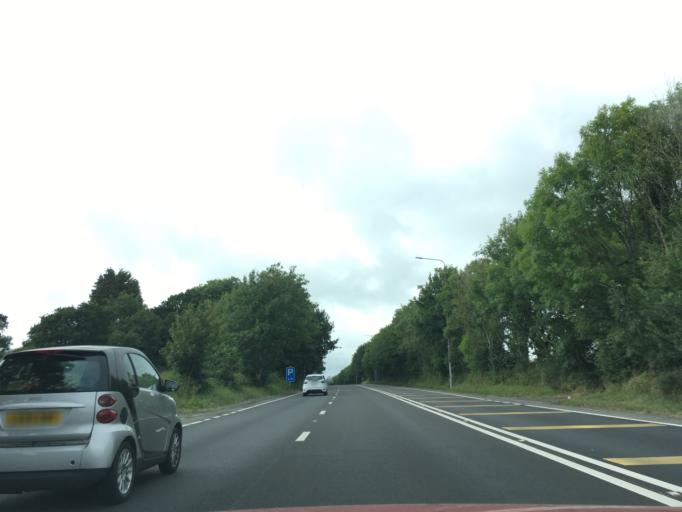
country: GB
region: Wales
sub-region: Carmarthenshire
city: Saint Clears
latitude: 51.8177
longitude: -4.5087
